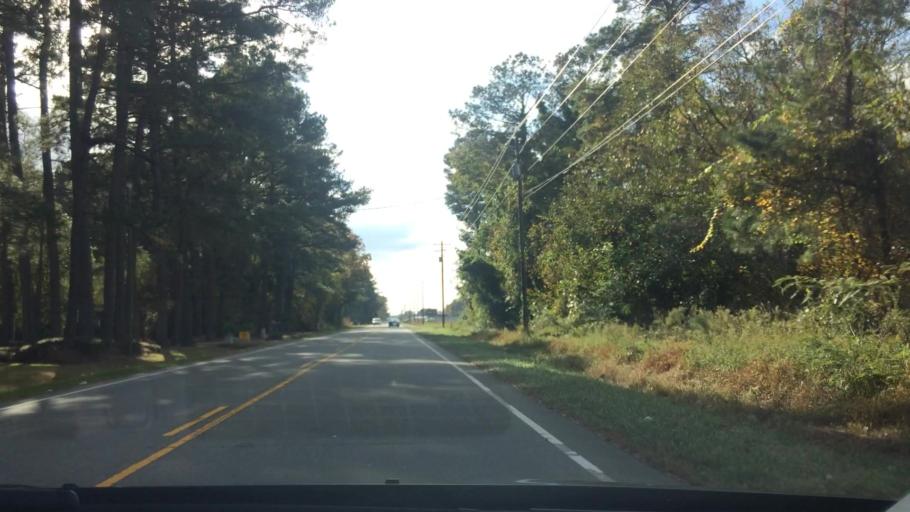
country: US
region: North Carolina
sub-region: Wayne County
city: Elroy
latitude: 35.4347
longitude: -77.8665
